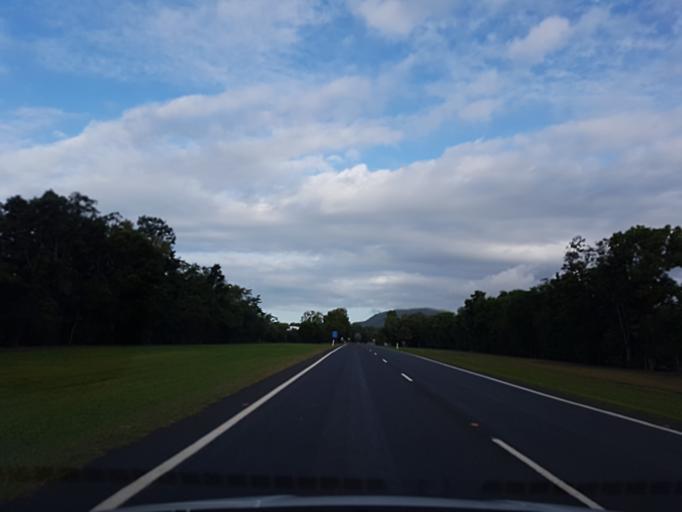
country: AU
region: Queensland
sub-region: Cairns
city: Port Douglas
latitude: -16.5322
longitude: 145.4650
